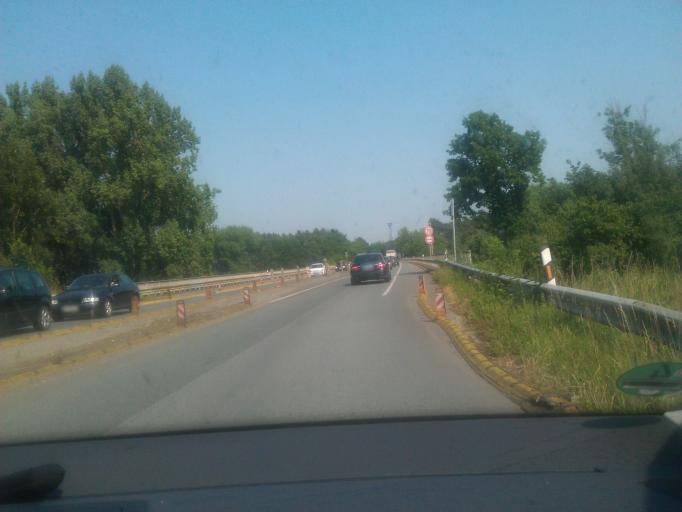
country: DE
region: North Rhine-Westphalia
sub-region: Regierungsbezirk Detmold
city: Bad Salzuflen
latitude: 52.0522
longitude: 8.7406
